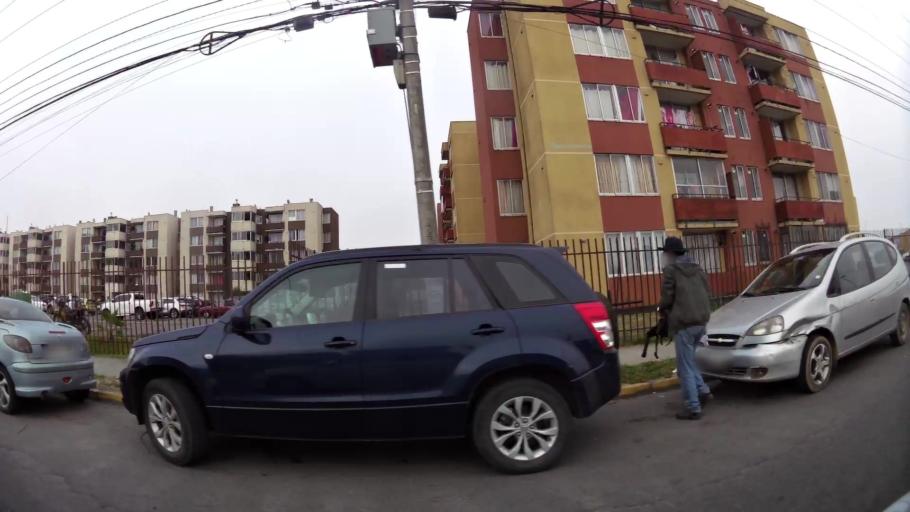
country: CL
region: Biobio
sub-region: Provincia de Concepcion
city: Concepcion
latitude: -36.7865
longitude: -73.0801
